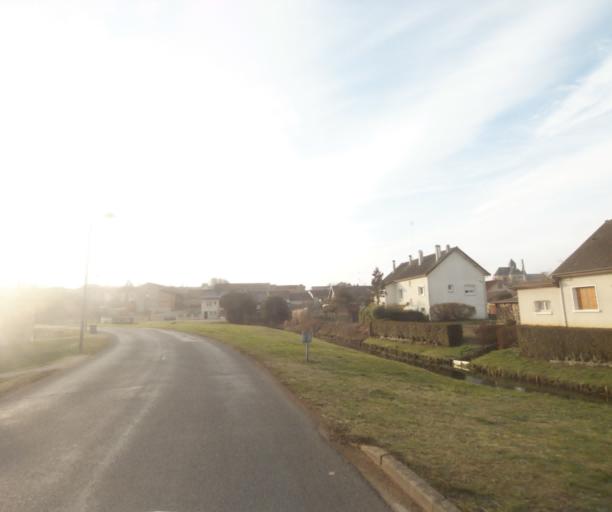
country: FR
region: Champagne-Ardenne
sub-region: Departement de la Marne
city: Sermaize-les-Bains
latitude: 48.7390
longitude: 4.9064
